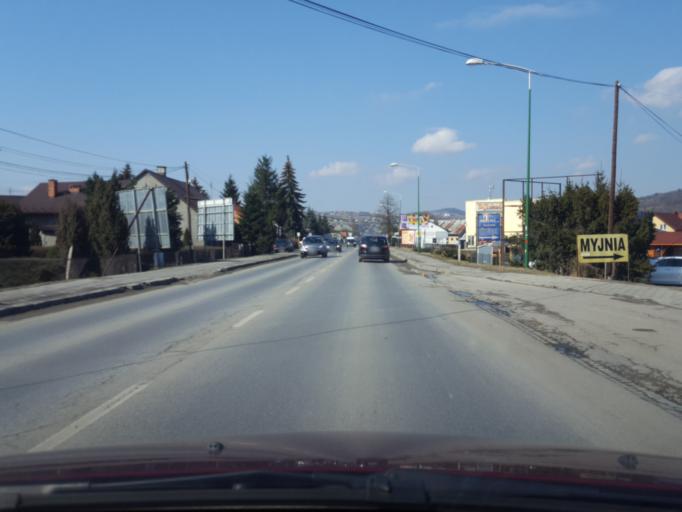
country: PL
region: Lesser Poland Voivodeship
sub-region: Powiat nowosadecki
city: Chelmiec
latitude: 49.6296
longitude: 20.6751
